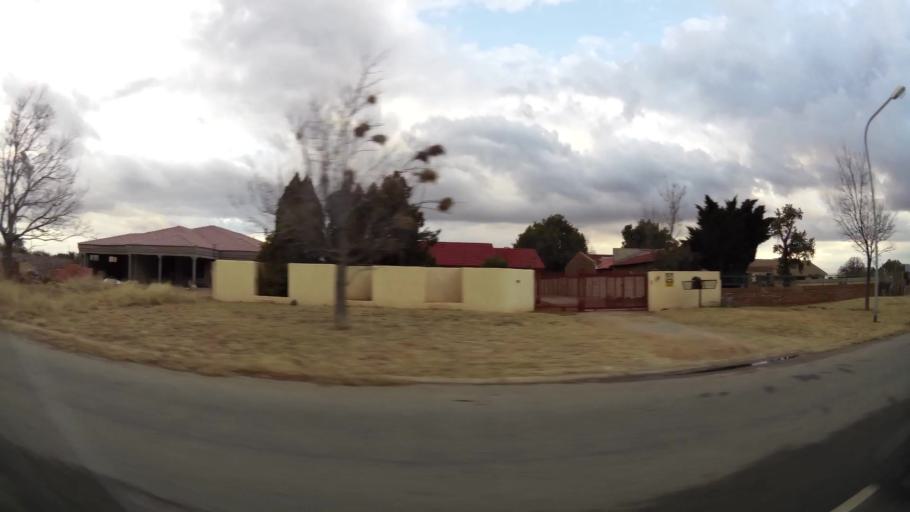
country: ZA
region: Orange Free State
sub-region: Lejweleputswa District Municipality
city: Welkom
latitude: -27.9440
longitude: 26.7317
